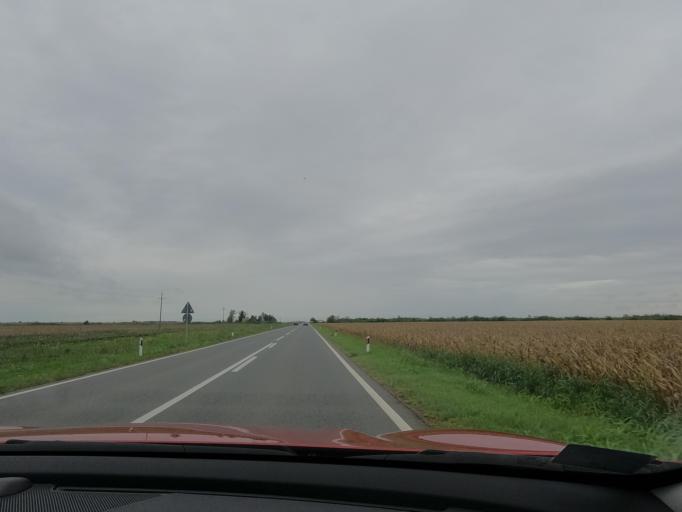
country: RS
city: Banatska Topola
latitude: 45.7143
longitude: 20.4179
